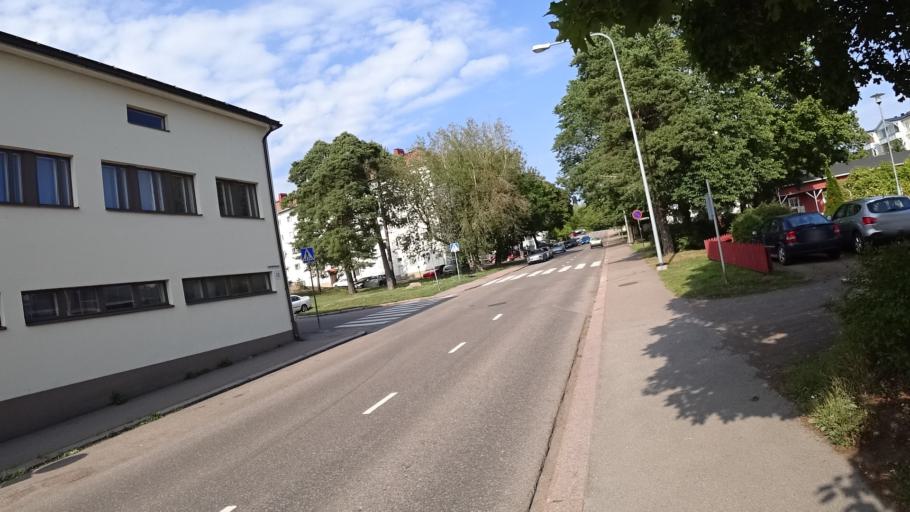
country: FI
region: Kymenlaakso
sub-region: Kotka-Hamina
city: Kotka
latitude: 60.4630
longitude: 26.9510
